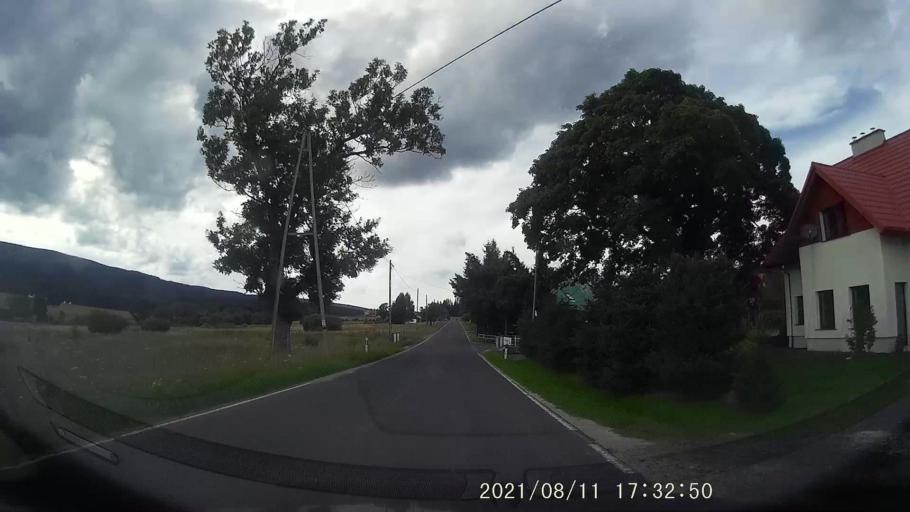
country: PL
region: Lower Silesian Voivodeship
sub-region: Powiat klodzki
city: Szczytna
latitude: 50.3117
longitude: 16.4489
